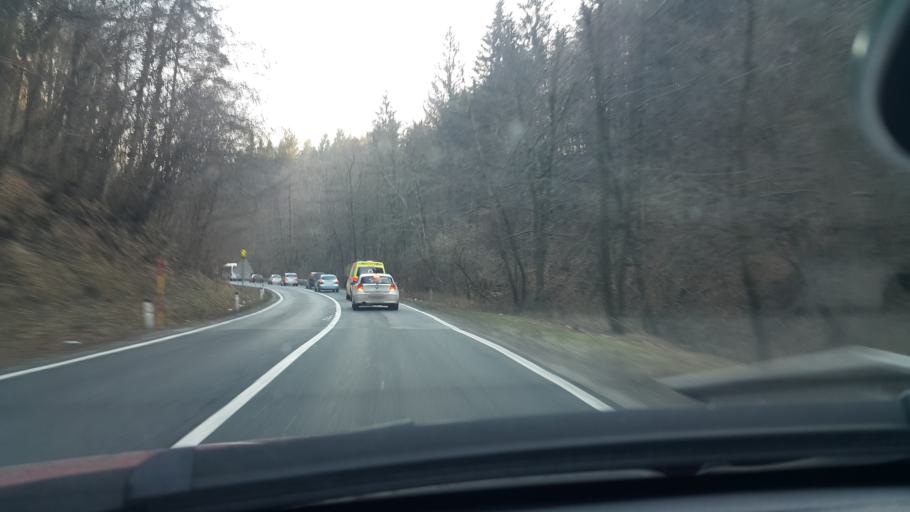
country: SI
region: Dobrna
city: Dobrna
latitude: 46.3294
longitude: 15.1768
